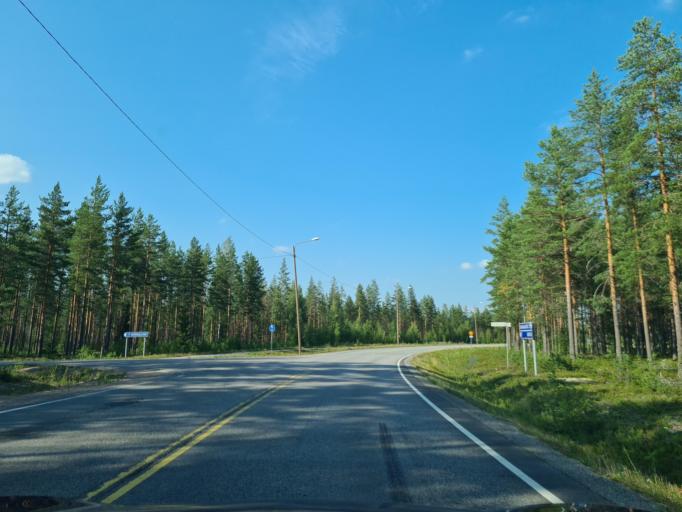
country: FI
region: Satakunta
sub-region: Pohjois-Satakunta
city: Karvia
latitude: 62.0737
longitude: 22.5065
